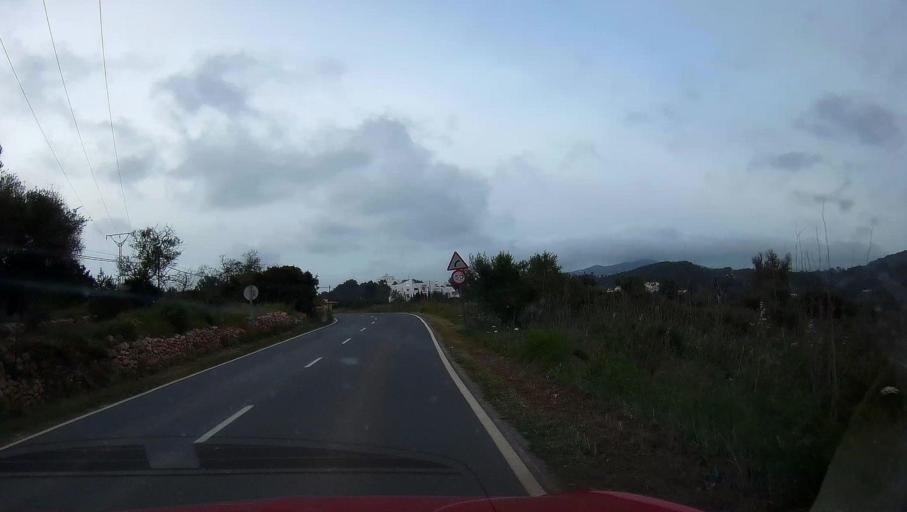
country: ES
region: Balearic Islands
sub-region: Illes Balears
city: Sant Joan de Labritja
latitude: 39.0517
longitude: 1.4338
